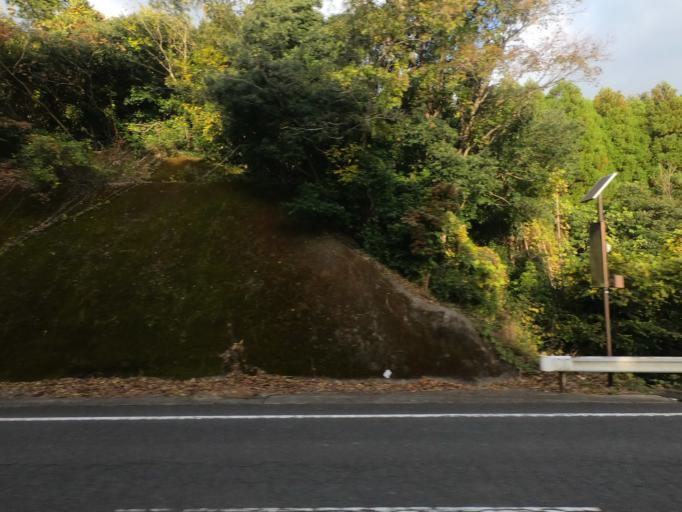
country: JP
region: Kumamoto
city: Minamata
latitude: 32.2430
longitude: 130.4800
